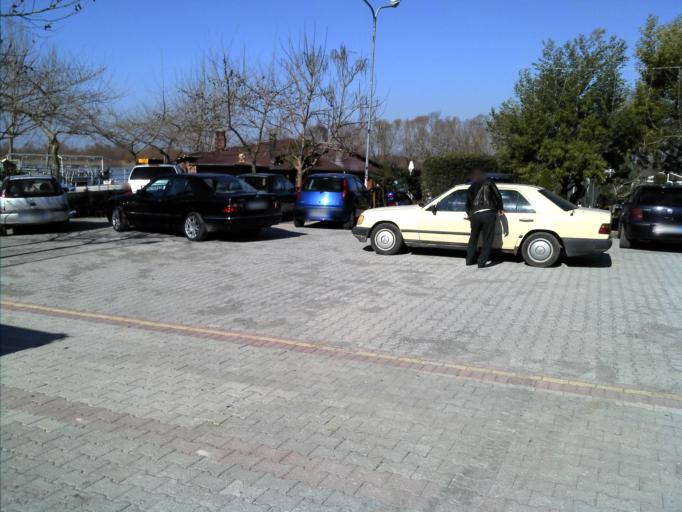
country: AL
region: Shkoder
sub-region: Rrethi i Shkodres
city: Shkoder
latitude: 42.0544
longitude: 19.4882
